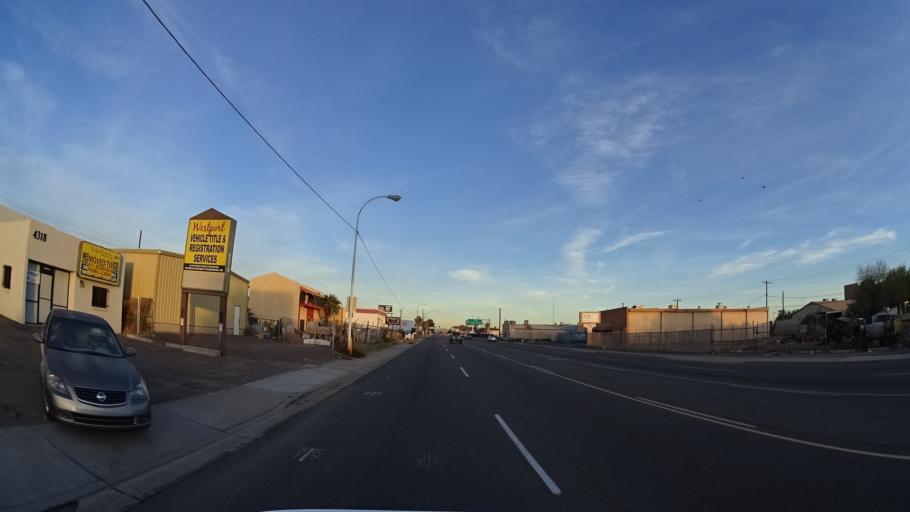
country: US
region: Arizona
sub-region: Maricopa County
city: Tempe Junction
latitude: 33.4220
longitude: -111.9882
